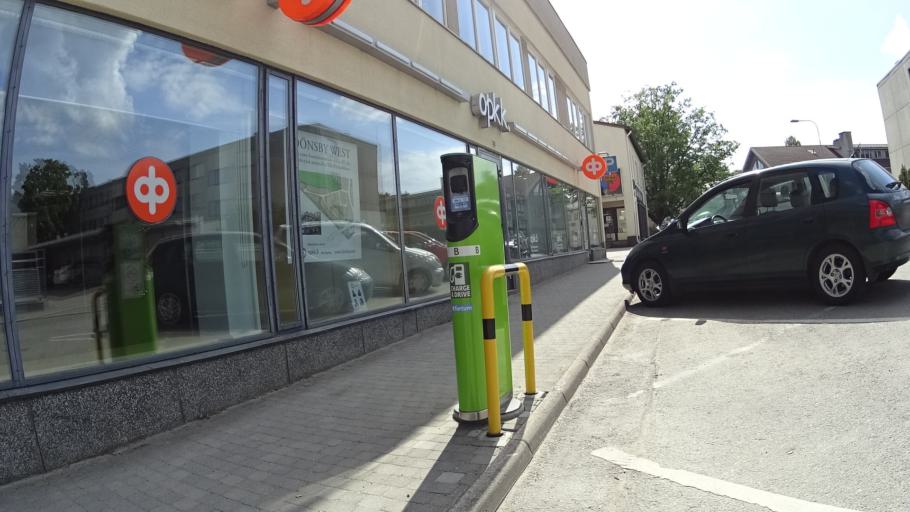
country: FI
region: Uusimaa
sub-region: Raaseporin
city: Karis
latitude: 60.0701
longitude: 23.6596
